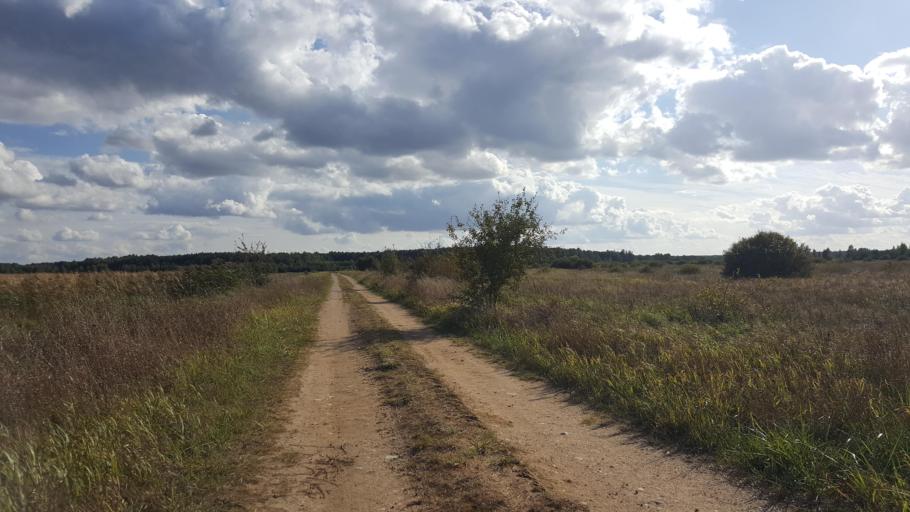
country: BY
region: Brest
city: Kamyanyets
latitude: 52.4486
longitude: 23.9347
